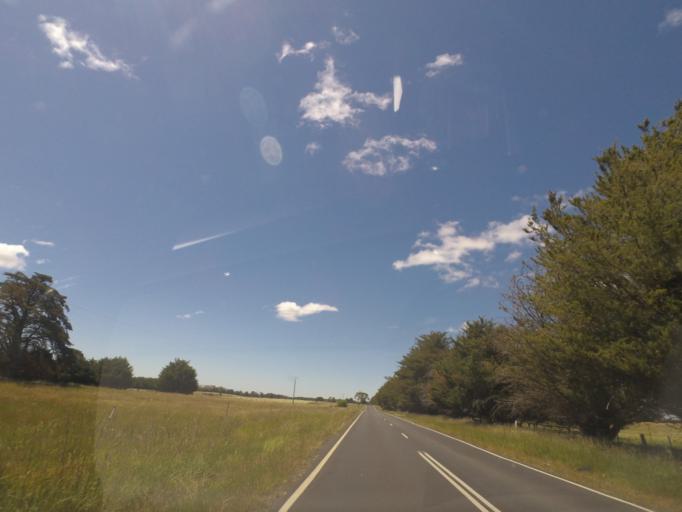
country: AU
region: Victoria
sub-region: Mount Alexander
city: Castlemaine
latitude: -37.2495
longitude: 144.3206
